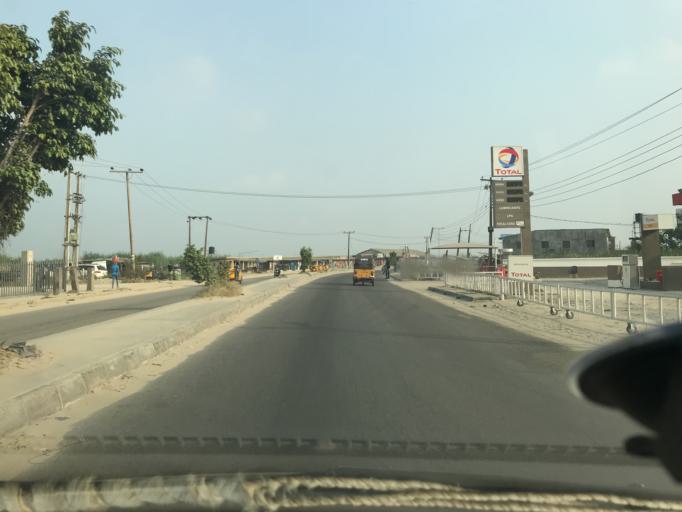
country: NG
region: Lagos
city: Ikoyi
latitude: 6.4764
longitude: 3.5682
